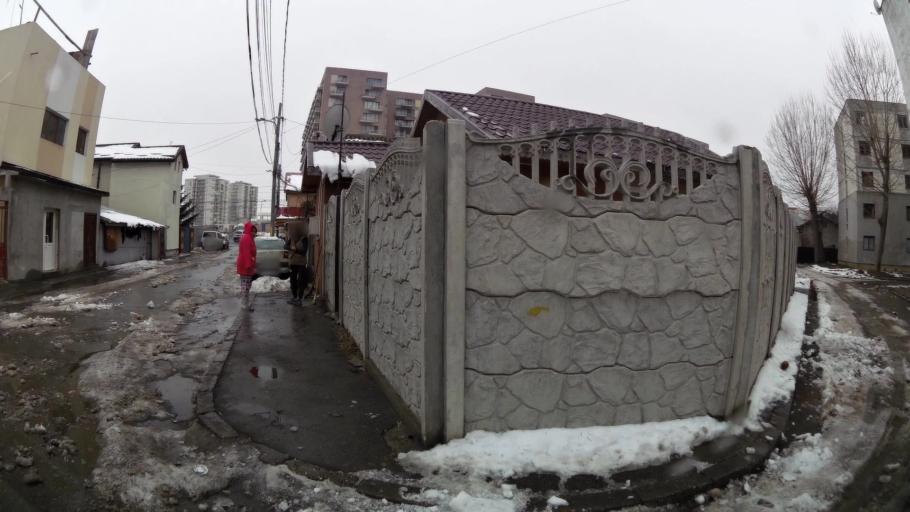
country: RO
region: Ilfov
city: Dobroesti
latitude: 44.4232
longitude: 26.1821
